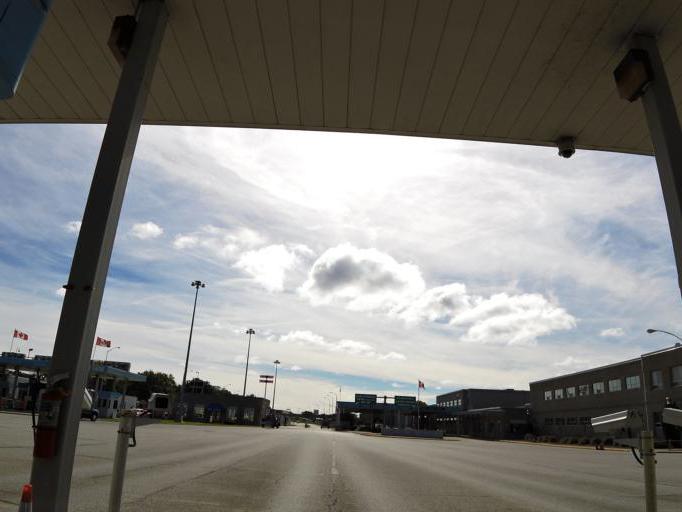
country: CA
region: Ontario
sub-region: Lambton County
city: Sarnia
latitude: 42.9934
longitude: -82.4119
